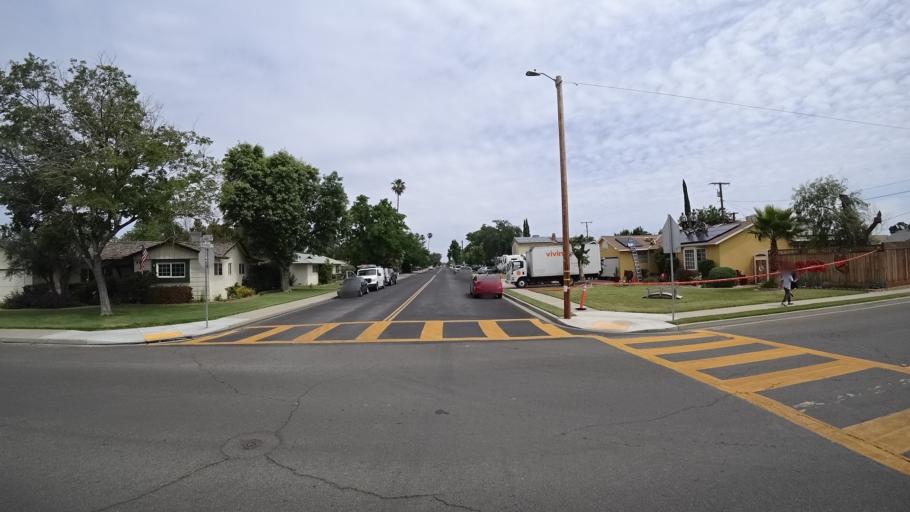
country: US
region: California
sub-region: Kings County
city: Hanford
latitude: 36.3498
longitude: -119.6397
